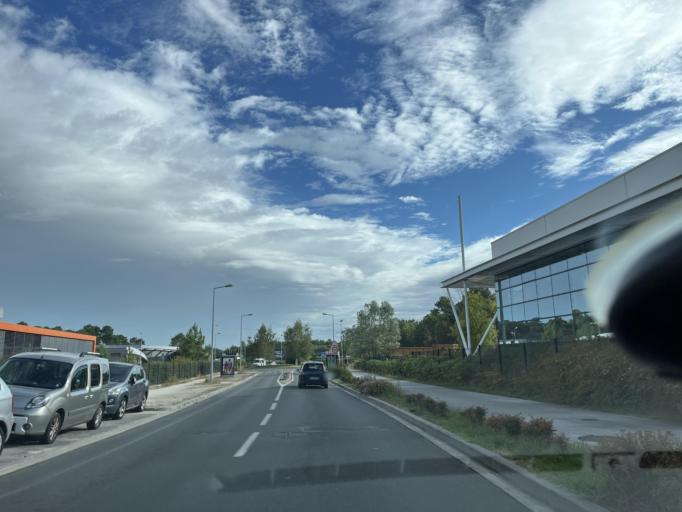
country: FR
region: Aquitaine
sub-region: Departement de la Gironde
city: Le Haillan
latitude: 44.8704
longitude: -0.6618
